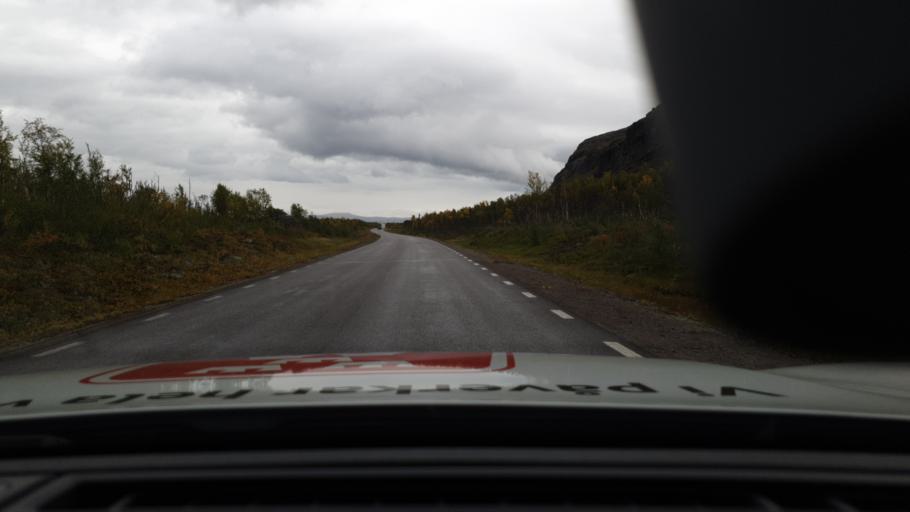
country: NO
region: Troms
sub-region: Bardu
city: Setermoen
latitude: 68.4263
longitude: 18.3590
